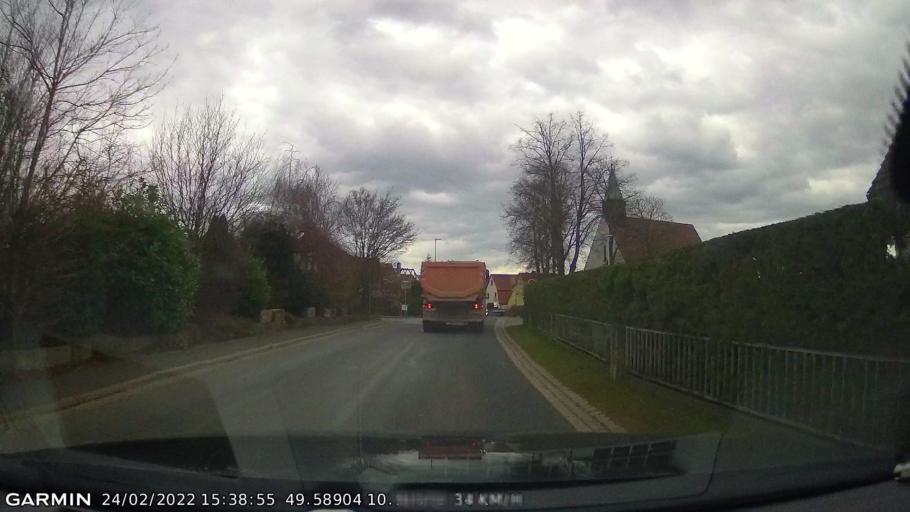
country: DE
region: Bavaria
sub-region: Regierungsbezirk Mittelfranken
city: Herzogenaurach
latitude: 49.5890
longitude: 10.9157
